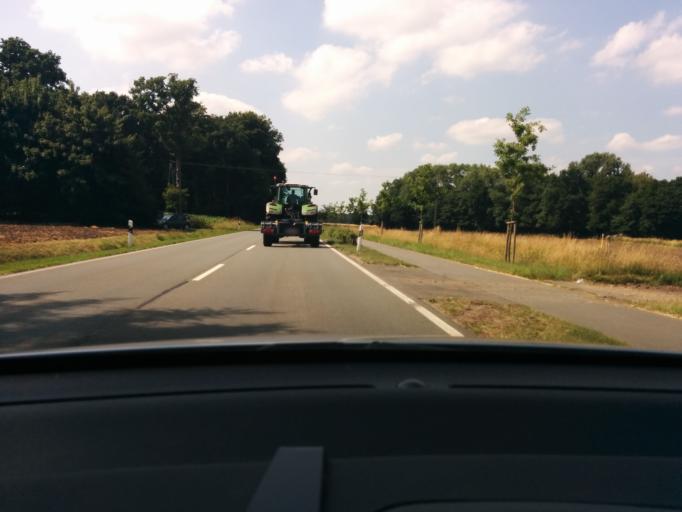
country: DE
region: North Rhine-Westphalia
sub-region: Regierungsbezirk Munster
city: Wettringen
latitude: 52.1771
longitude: 7.2801
